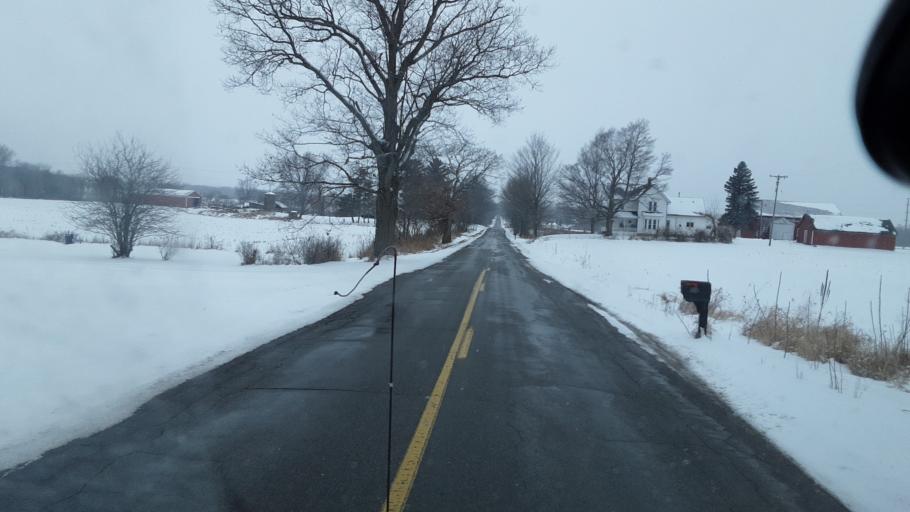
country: US
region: Michigan
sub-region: Ingham County
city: Leslie
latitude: 42.4367
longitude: -84.4677
